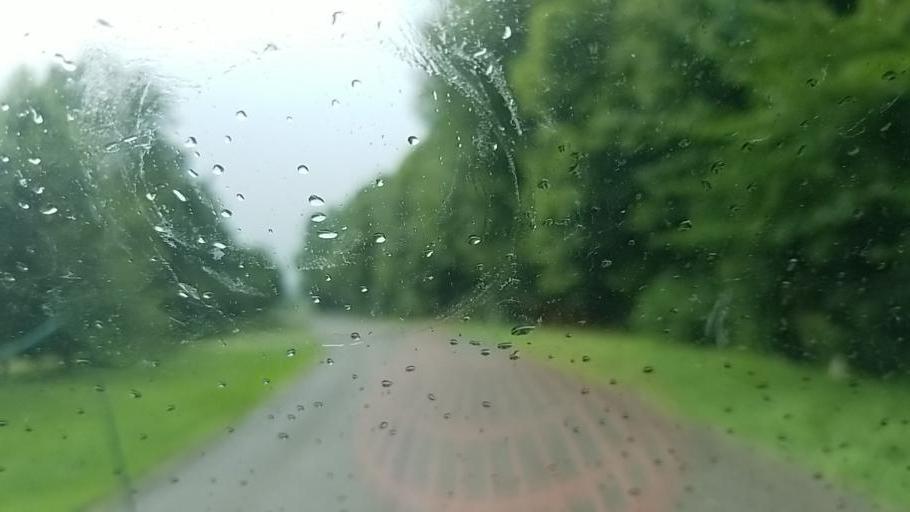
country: US
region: Ohio
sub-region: Champaign County
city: North Lewisburg
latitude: 40.3177
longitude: -83.6324
